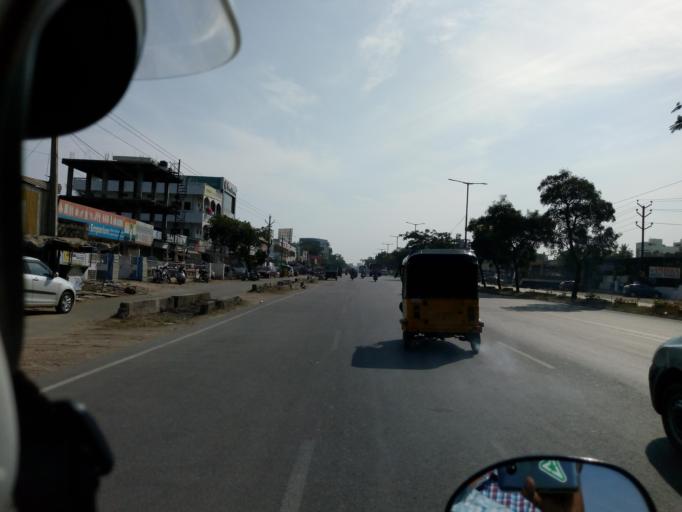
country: IN
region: Telangana
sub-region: Rangareddi
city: Lal Bahadur Nagar
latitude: 17.3719
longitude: 78.5577
